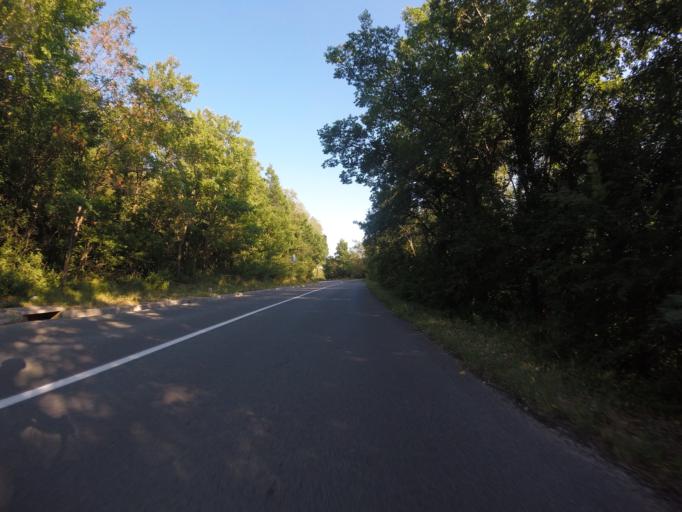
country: HR
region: Primorsko-Goranska
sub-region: Grad Crikvenica
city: Crikvenica
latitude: 45.2051
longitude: 14.7152
